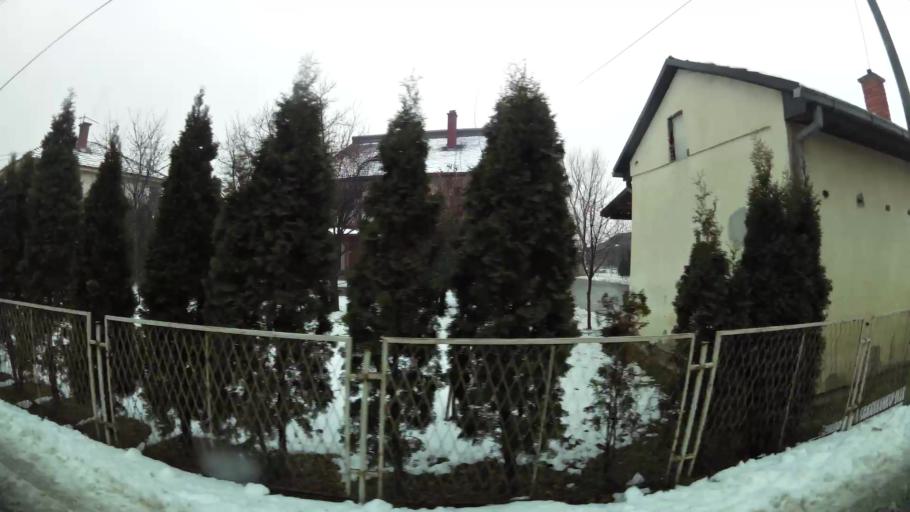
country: MK
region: Petrovec
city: Petrovec
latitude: 41.9382
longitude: 21.6143
